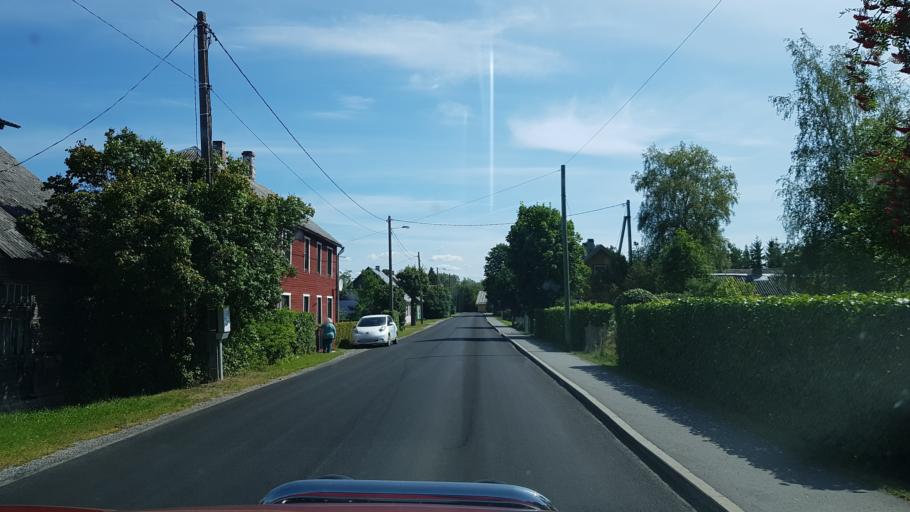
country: EE
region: Laeaene-Virumaa
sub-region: Tapa vald
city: Tapa
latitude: 59.1934
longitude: 25.8284
